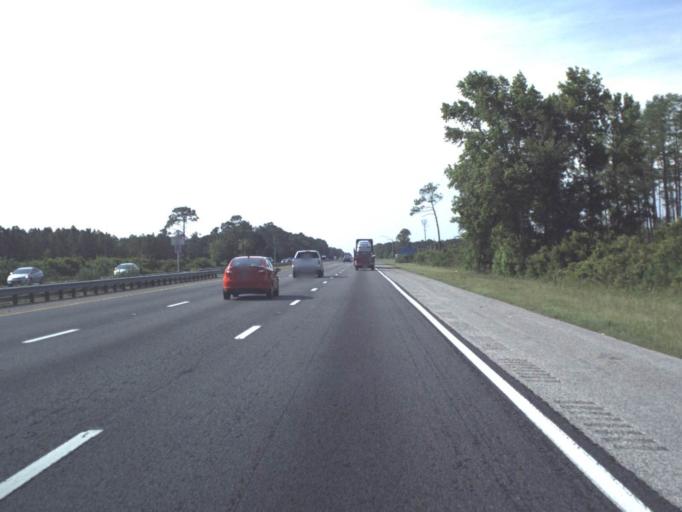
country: US
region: Florida
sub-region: Saint Johns County
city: Saint Augustine Shores
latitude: 29.6938
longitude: -81.3247
